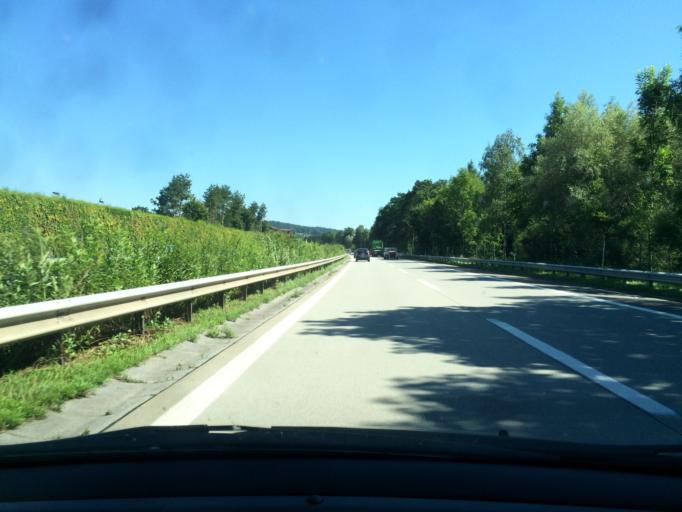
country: CH
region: Saint Gallen
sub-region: Wahlkreis Rheintal
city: Ruthi
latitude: 47.2852
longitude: 9.5485
